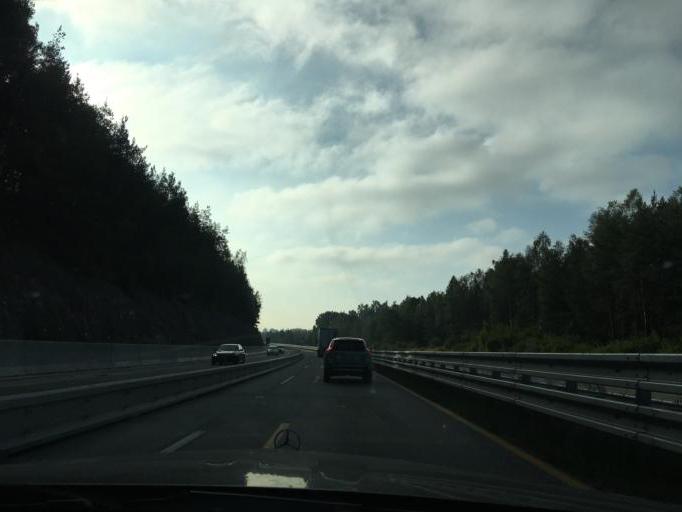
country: CZ
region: Central Bohemia
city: Trhovy Stepanov
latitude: 49.7466
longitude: 15.0299
